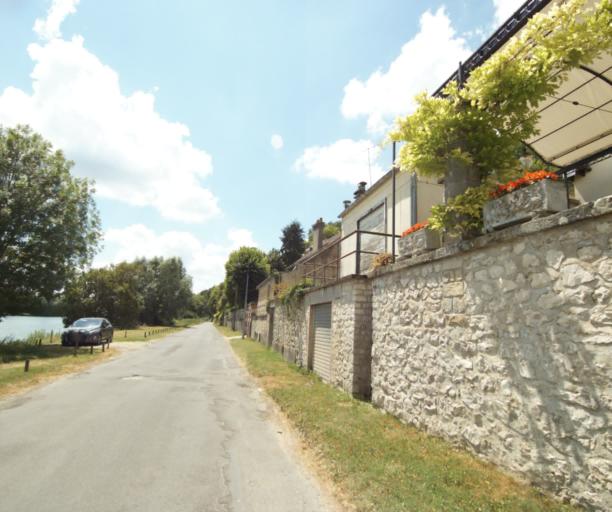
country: FR
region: Ile-de-France
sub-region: Departement de Seine-et-Marne
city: Samois-sur-Seine
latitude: 48.4459
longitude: 2.7512
